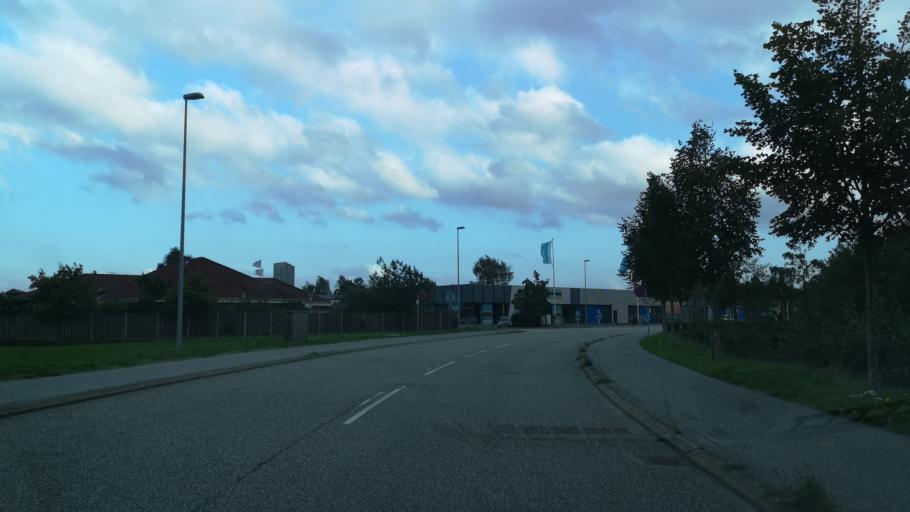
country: DK
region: Central Jutland
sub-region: Herning Kommune
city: Herning
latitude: 56.1360
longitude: 9.0071
